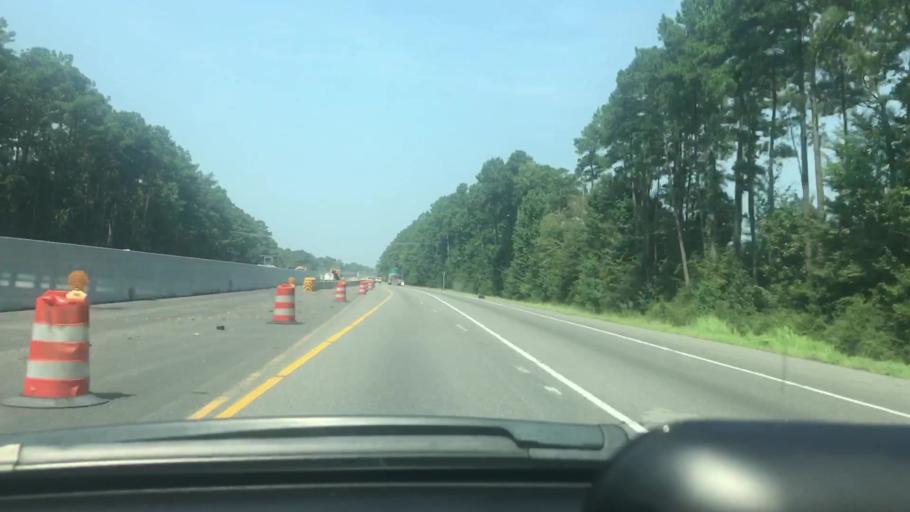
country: US
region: Louisiana
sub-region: Livingston Parish
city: Livingston
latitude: 30.4741
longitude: -90.7880
